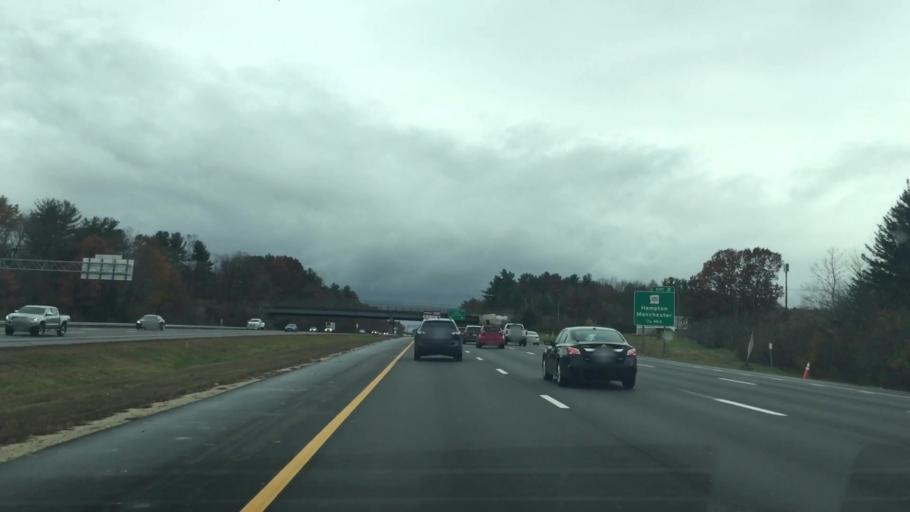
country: US
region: New Hampshire
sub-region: Rockingham County
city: Hampton
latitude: 42.9398
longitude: -70.8609
